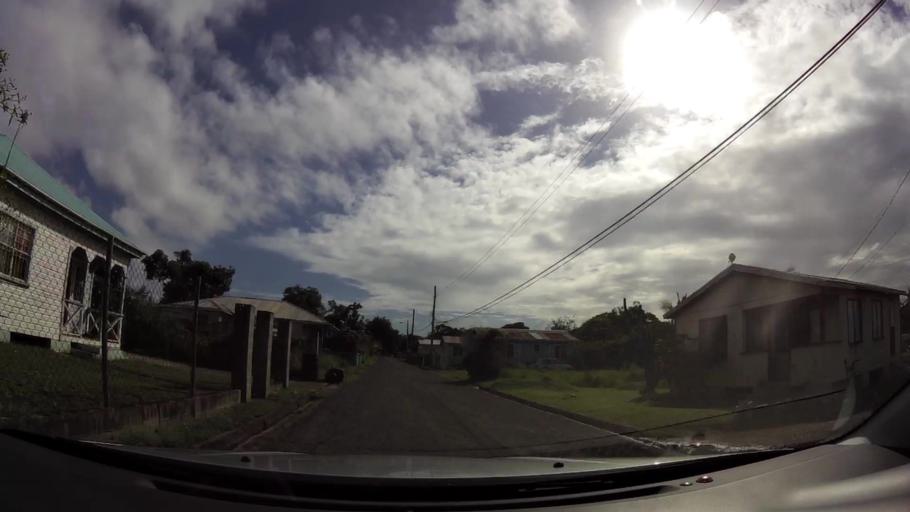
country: AG
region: Saint John
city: Saint John's
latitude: 17.1213
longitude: -61.8303
